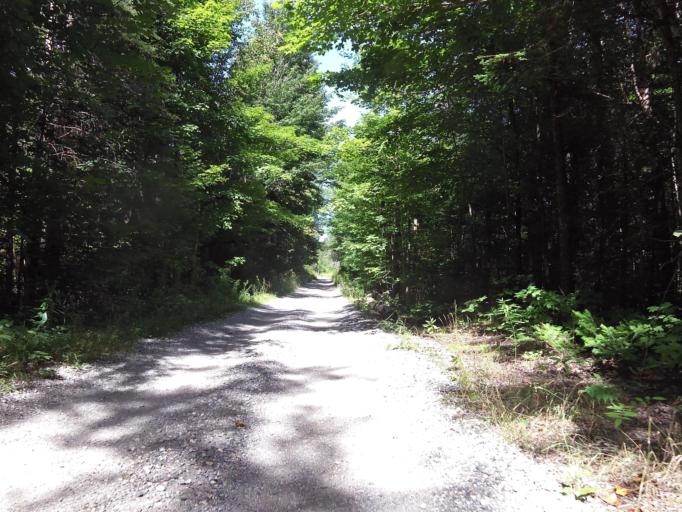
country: CA
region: Ontario
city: Renfrew
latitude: 45.0257
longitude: -76.7047
